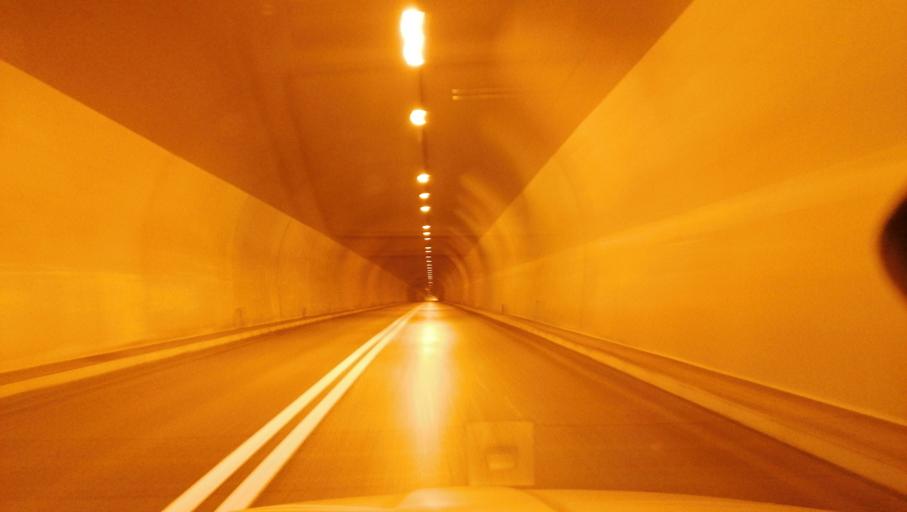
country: RS
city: Durici
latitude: 43.8287
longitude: 19.5220
